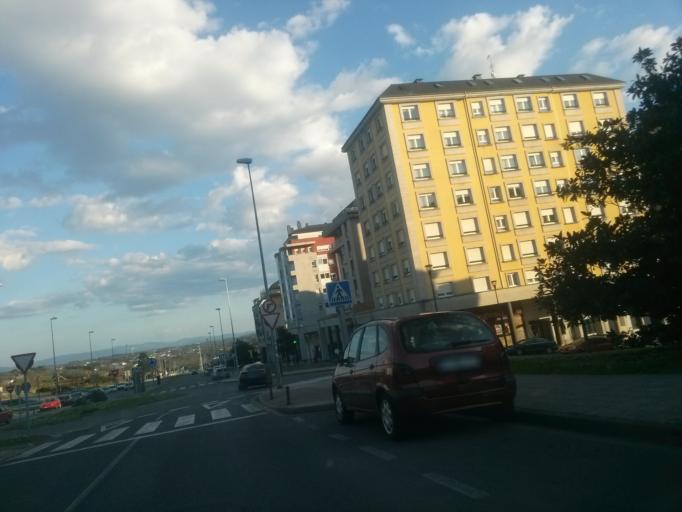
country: ES
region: Galicia
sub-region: Provincia de Lugo
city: Lugo
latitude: 42.9983
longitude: -7.5468
